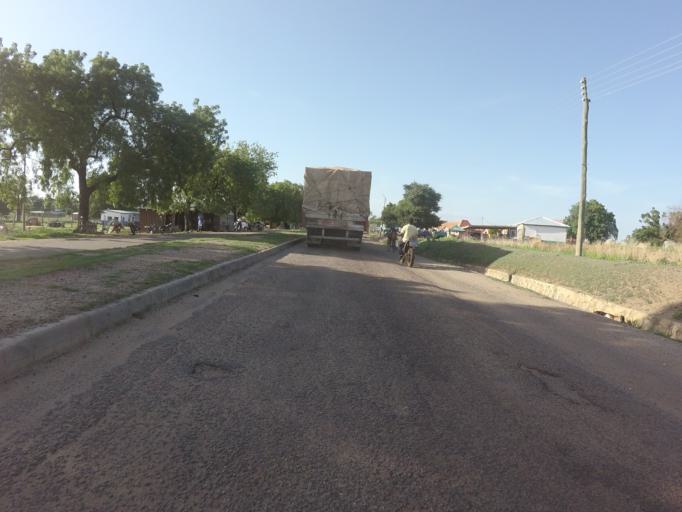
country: GH
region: Upper East
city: Navrongo
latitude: 10.9023
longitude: -1.0919
